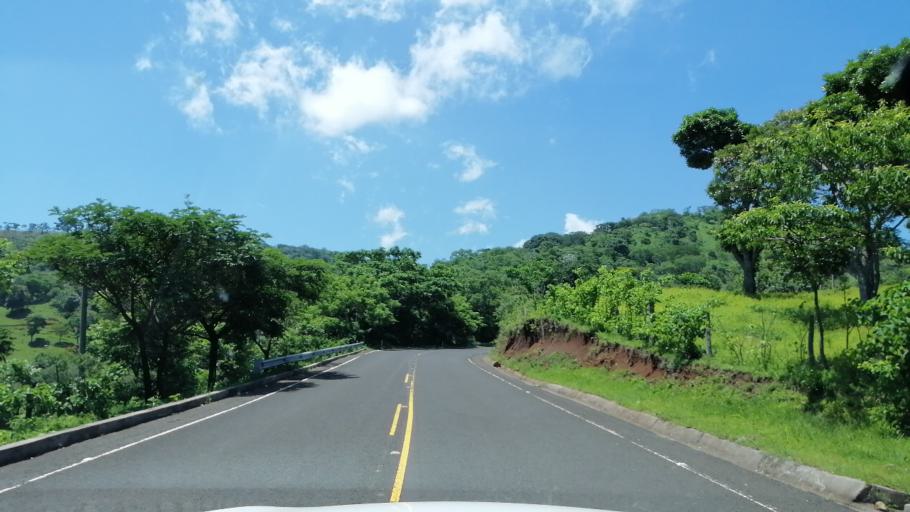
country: SV
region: San Miguel
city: Ciudad Barrios
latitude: 13.8029
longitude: -88.2997
